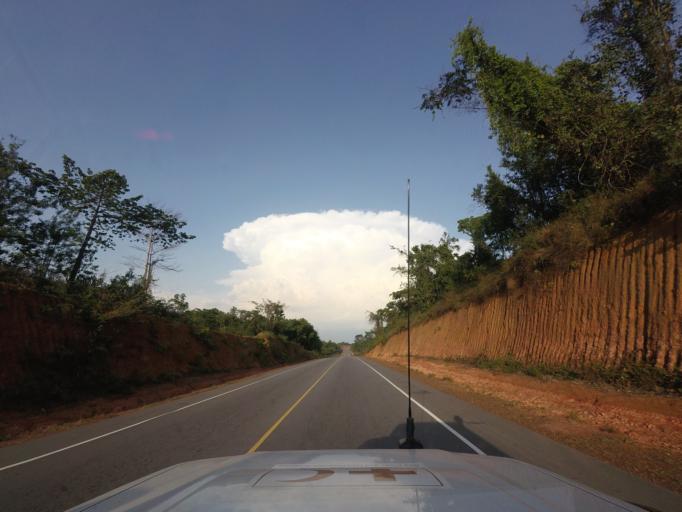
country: LR
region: Bong
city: Gbarnga
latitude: 7.0575
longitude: -9.2127
